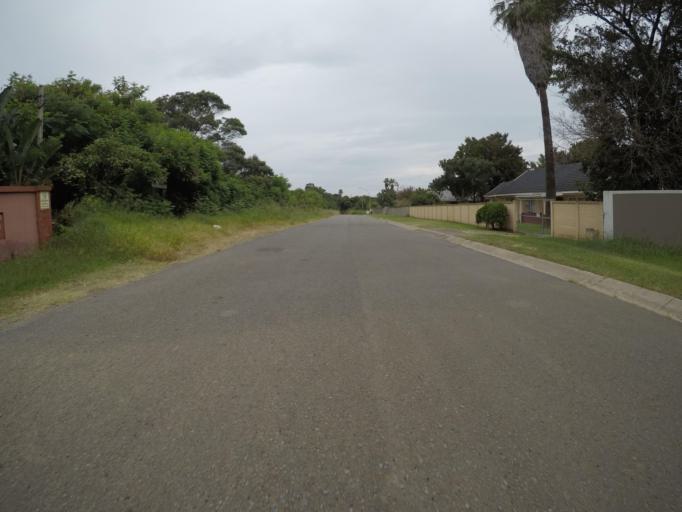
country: ZA
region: Eastern Cape
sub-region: Buffalo City Metropolitan Municipality
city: East London
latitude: -32.9956
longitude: 27.8580
